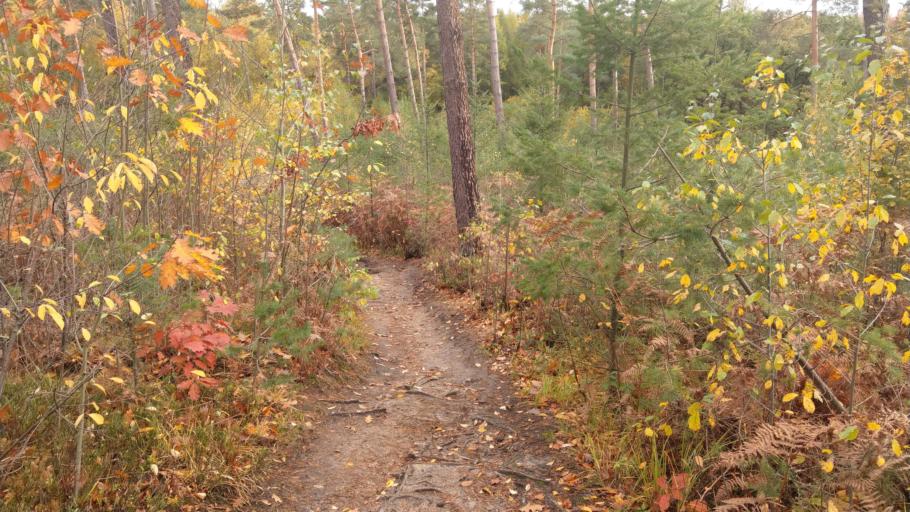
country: BE
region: Wallonia
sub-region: Province de Liege
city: La Calamine
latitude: 50.7319
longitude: 6.0220
